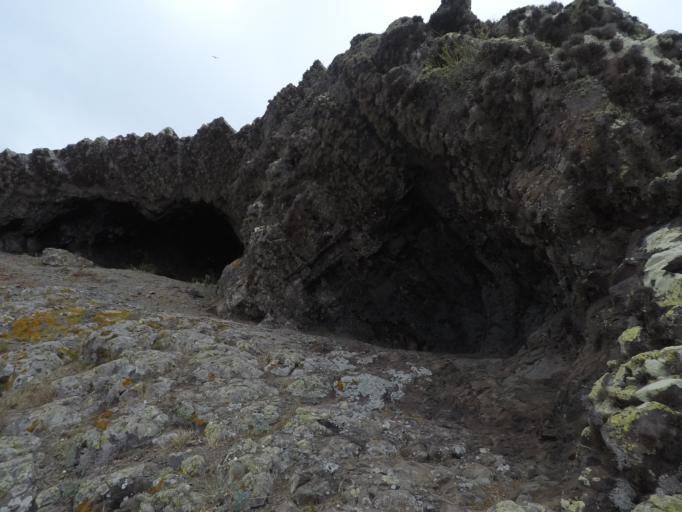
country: PT
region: Madeira
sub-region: Porto Santo
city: Vila de Porto Santo
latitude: 33.0467
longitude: -16.3685
